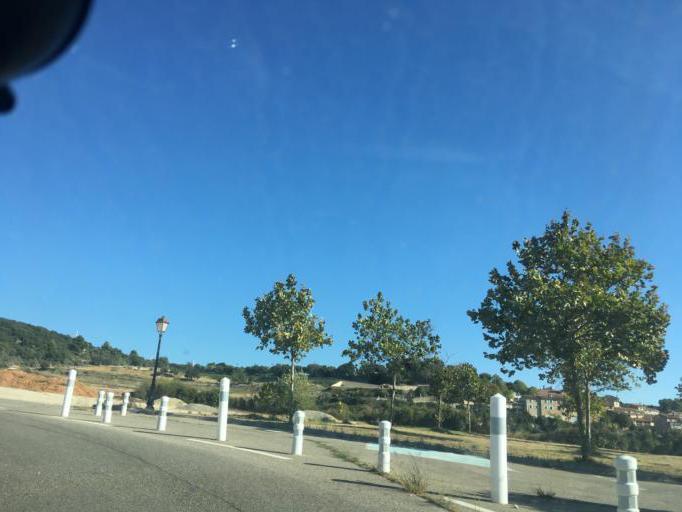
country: FR
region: Provence-Alpes-Cote d'Azur
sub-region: Departement du Var
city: Regusse
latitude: 43.7186
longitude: 6.1315
